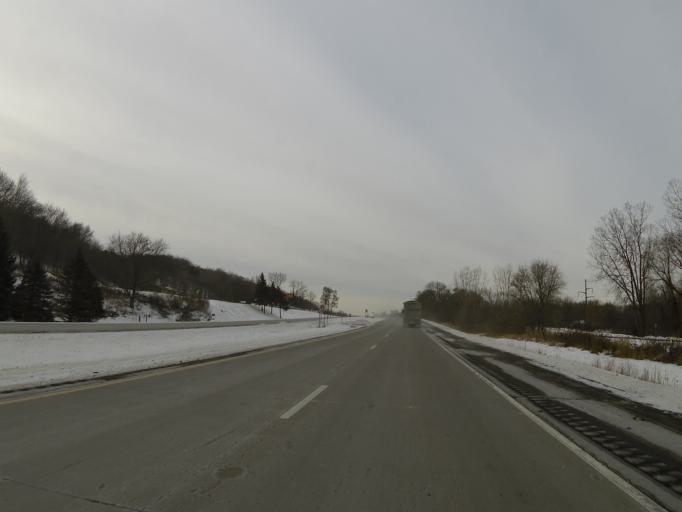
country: US
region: Minnesota
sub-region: Scott County
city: Jordan
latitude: 44.6917
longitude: -93.6047
